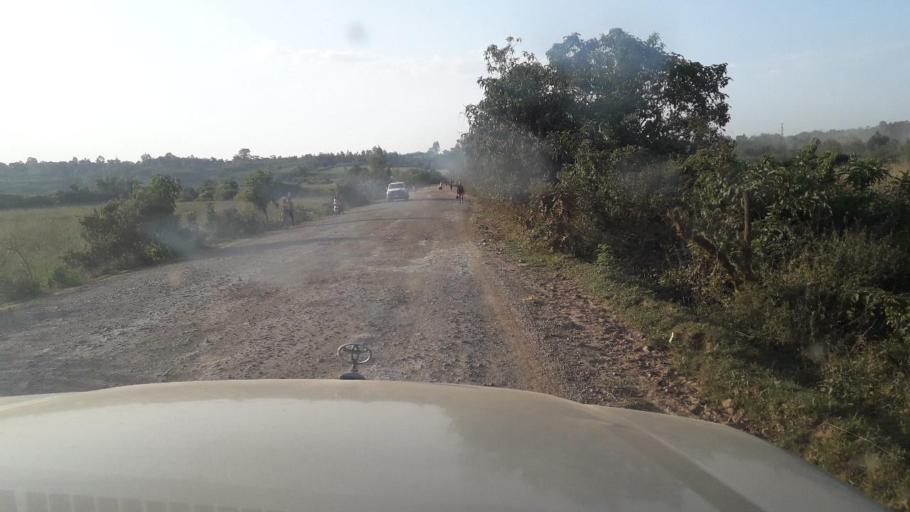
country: ET
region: Oromiya
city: Jima
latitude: 7.6121
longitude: 36.8358
